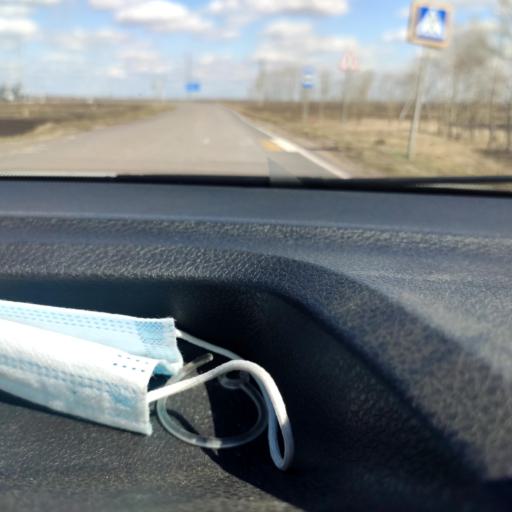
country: RU
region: Bashkortostan
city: Alekseyevka
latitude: 54.7805
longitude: 55.1800
